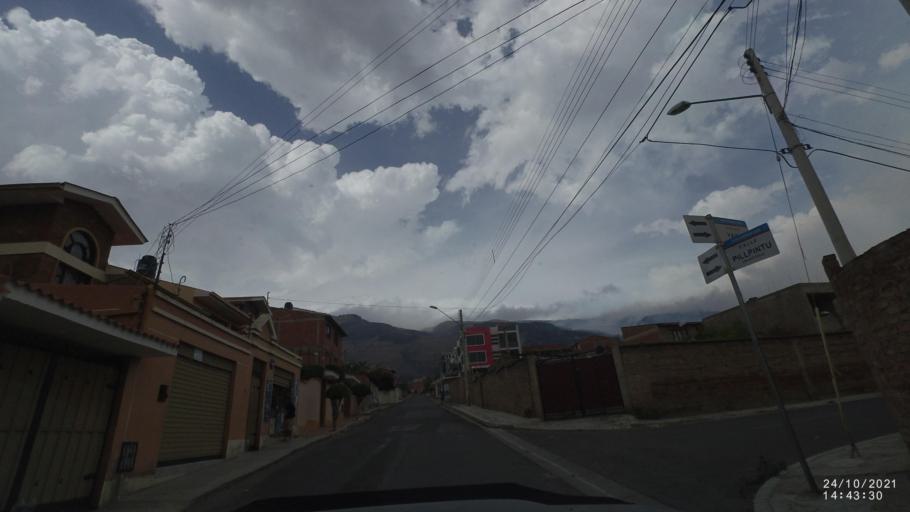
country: BO
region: Cochabamba
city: Cochabamba
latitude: -17.3474
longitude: -66.1753
